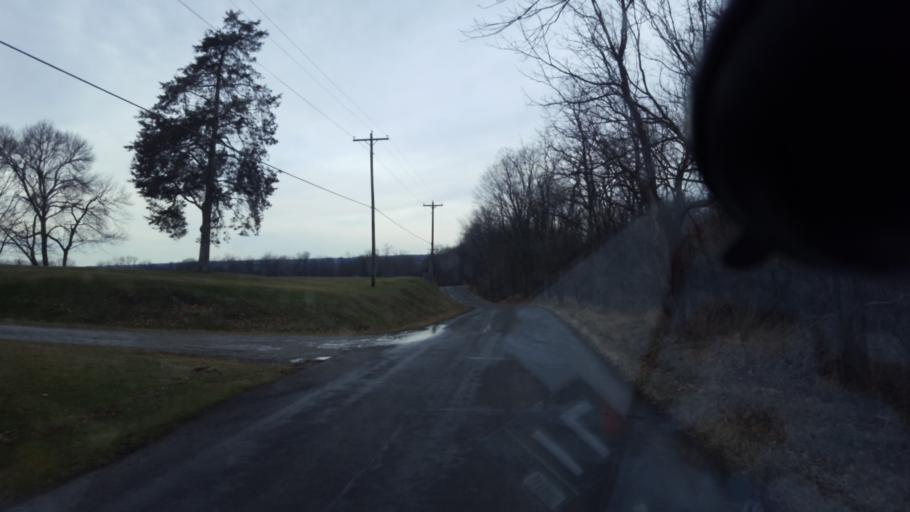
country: US
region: Ohio
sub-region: Wayne County
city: Wooster
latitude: 40.7312
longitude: -81.9272
